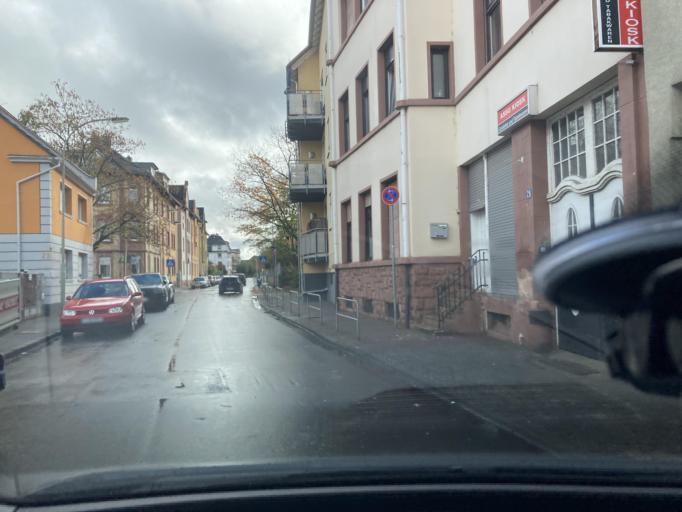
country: DE
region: Hesse
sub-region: Regierungsbezirk Darmstadt
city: Offenbach
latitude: 50.1208
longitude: 8.7689
